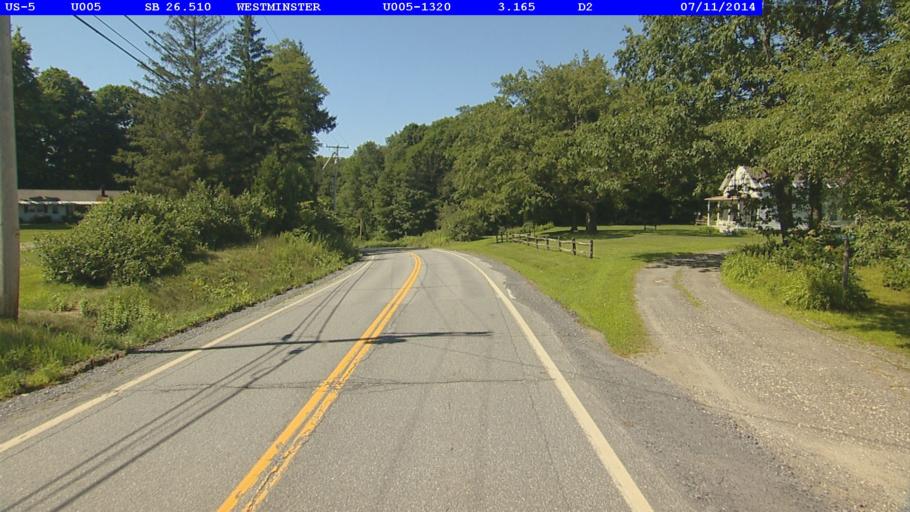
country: US
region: Vermont
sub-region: Windham County
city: Bellows Falls
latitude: 43.0633
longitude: -72.4637
